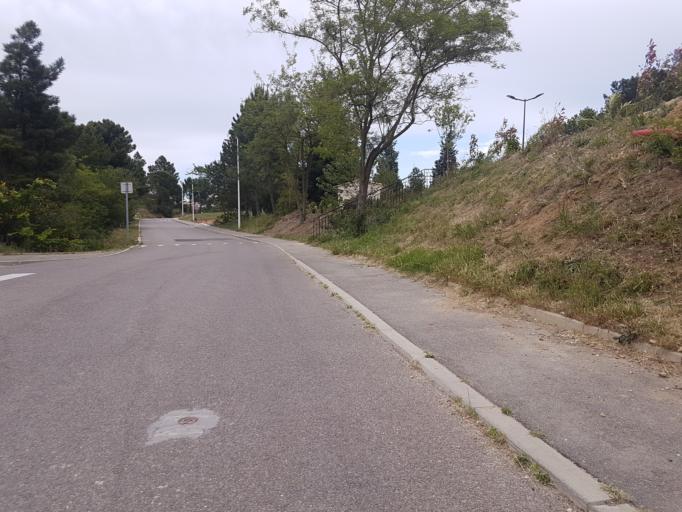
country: FR
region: Provence-Alpes-Cote d'Azur
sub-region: Departement du Vaucluse
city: Mondragon
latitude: 44.2405
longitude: 4.7180
